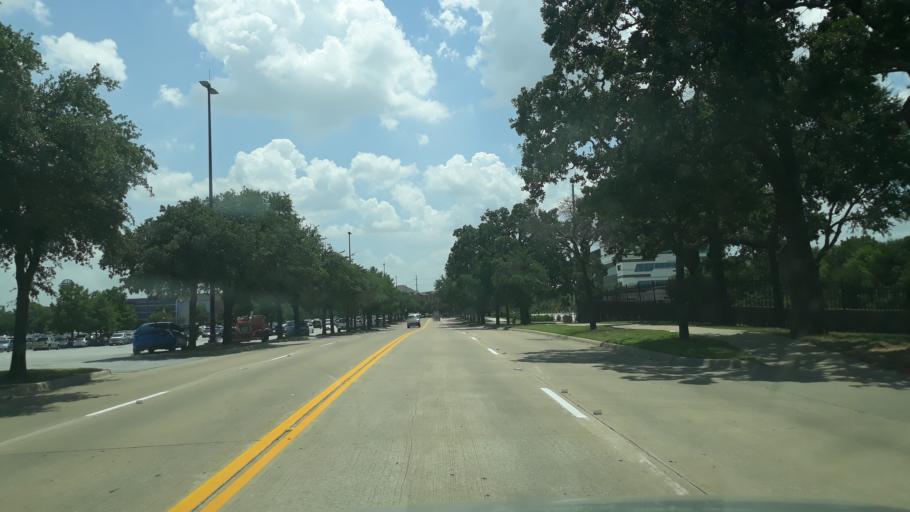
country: US
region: Texas
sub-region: Dallas County
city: Coppell
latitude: 32.9700
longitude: -97.0439
